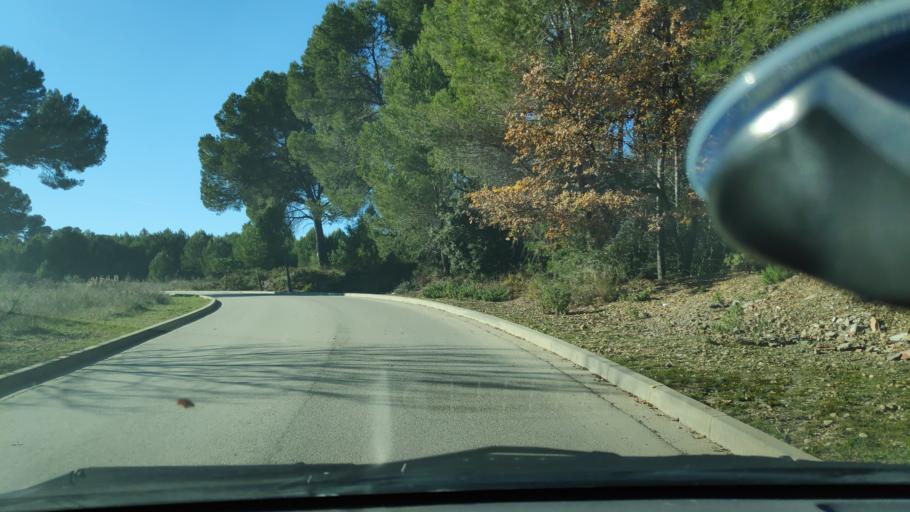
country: ES
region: Catalonia
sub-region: Provincia de Barcelona
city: Sant Quirze del Valles
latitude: 41.5380
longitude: 2.0555
